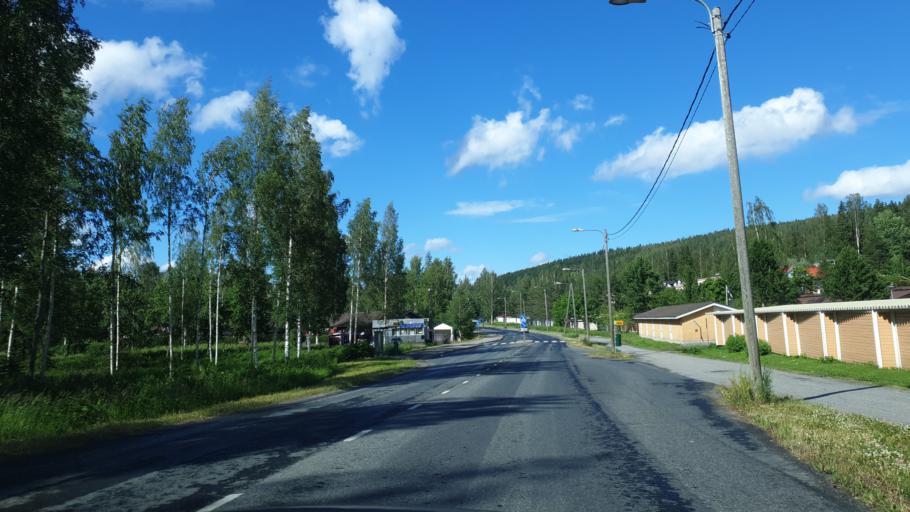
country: FI
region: Northern Savo
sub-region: Kuopio
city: Kuopio
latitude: 62.9216
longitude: 27.6308
